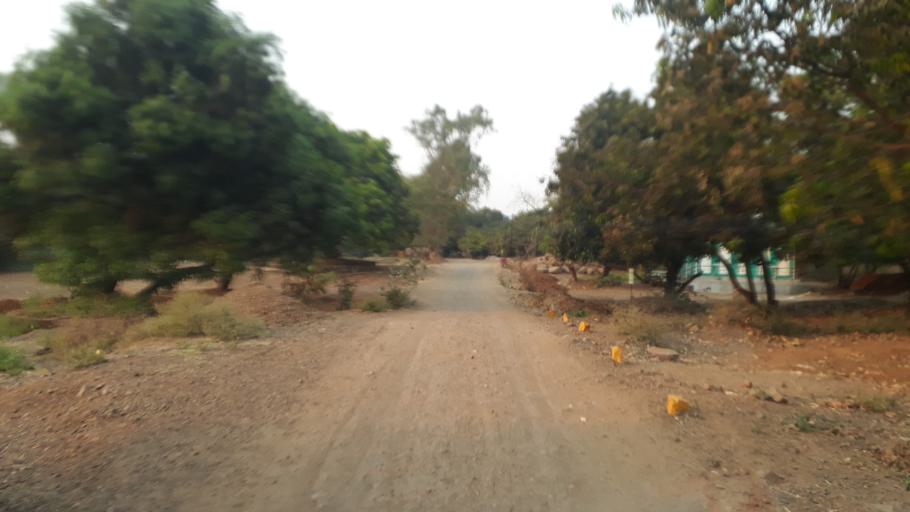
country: IN
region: Maharashtra
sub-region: Raigarh
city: Neral
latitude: 19.0417
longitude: 73.3243
